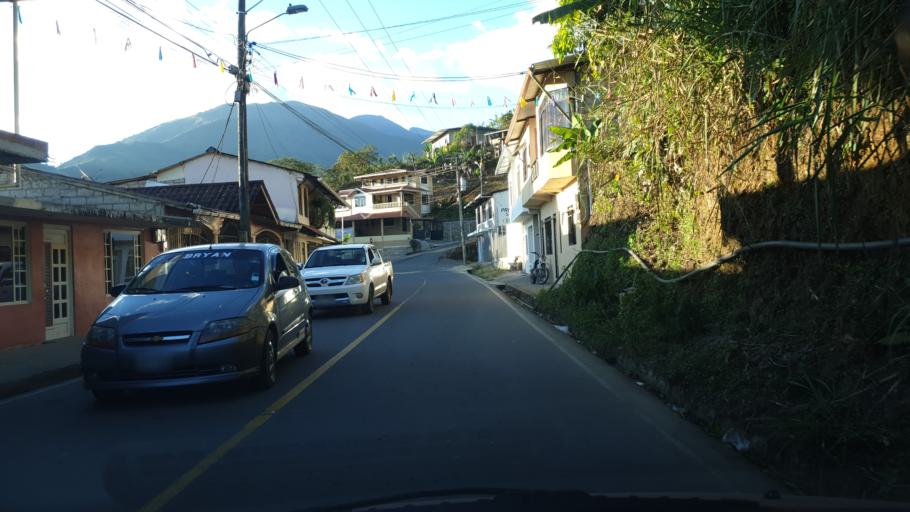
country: EC
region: El Oro
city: Zaruma
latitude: -3.6054
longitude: -79.6310
